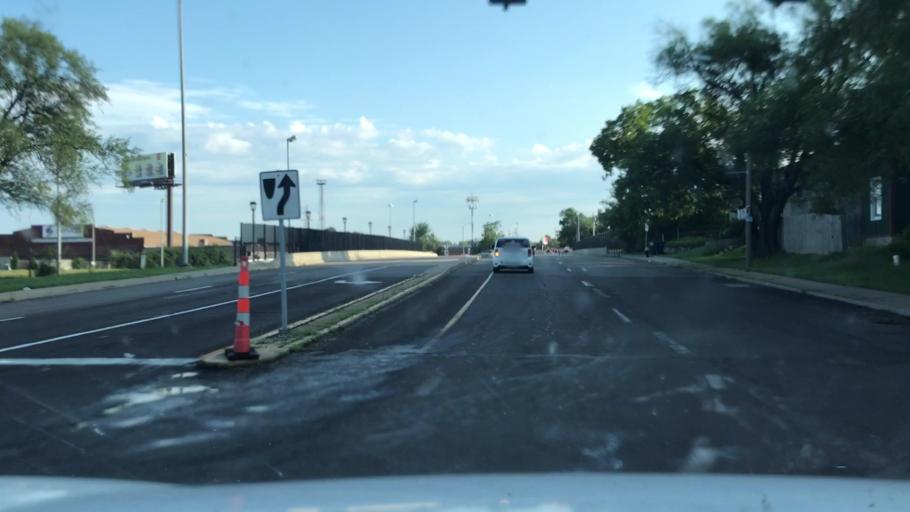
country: US
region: Missouri
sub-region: Saint Louis County
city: Maplewood
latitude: 38.6049
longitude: -90.3074
